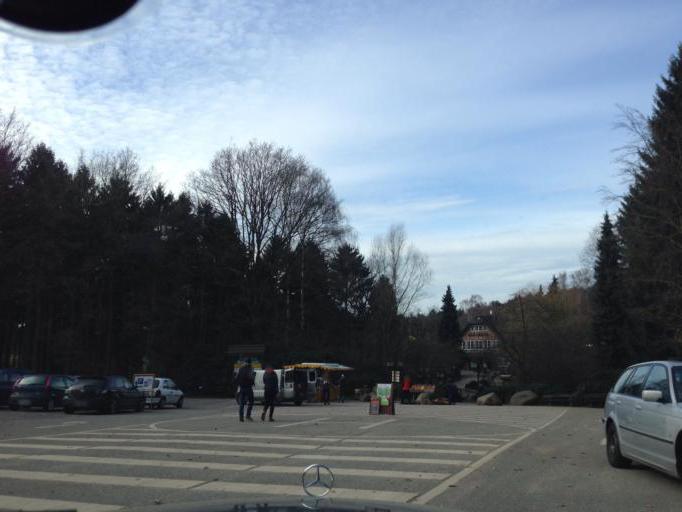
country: DE
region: Lower Saxony
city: Seevetal
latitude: 53.4418
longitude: 9.8875
